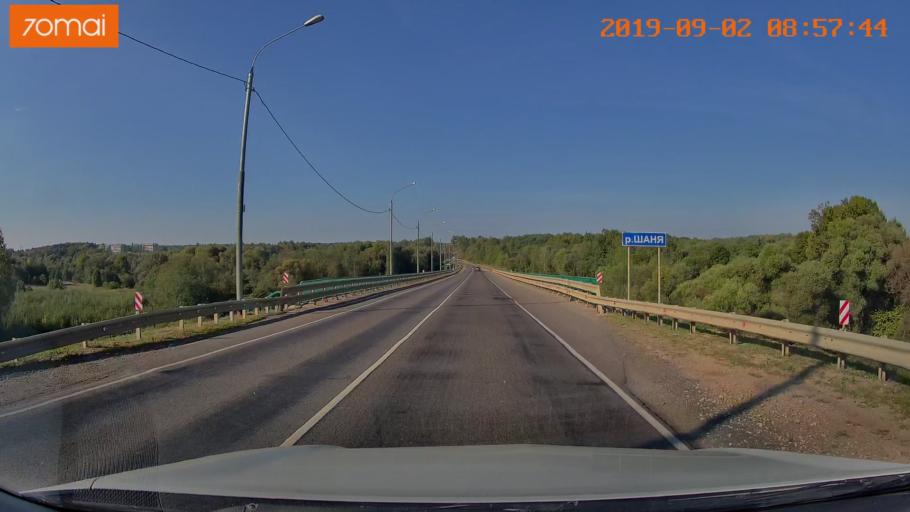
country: RU
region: Kaluga
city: Myatlevo
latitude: 54.9343
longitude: 35.7612
